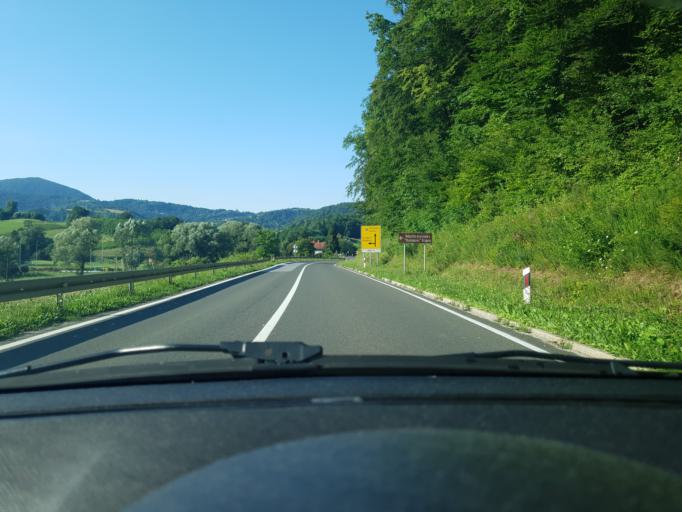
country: HR
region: Krapinsko-Zagorska
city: Radoboj
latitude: 46.1454
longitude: 15.9402
